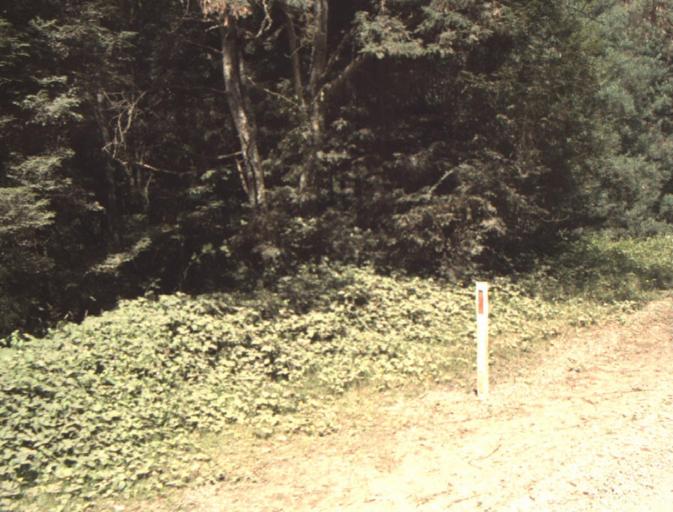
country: AU
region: Tasmania
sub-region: Dorset
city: Scottsdale
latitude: -41.3211
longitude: 147.4148
